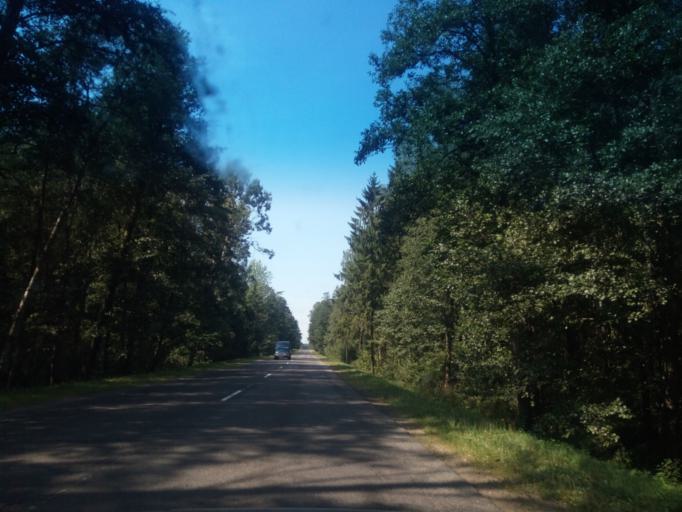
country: BY
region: Vitebsk
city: Vyerkhnyadzvinsk
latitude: 55.7951
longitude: 27.9627
